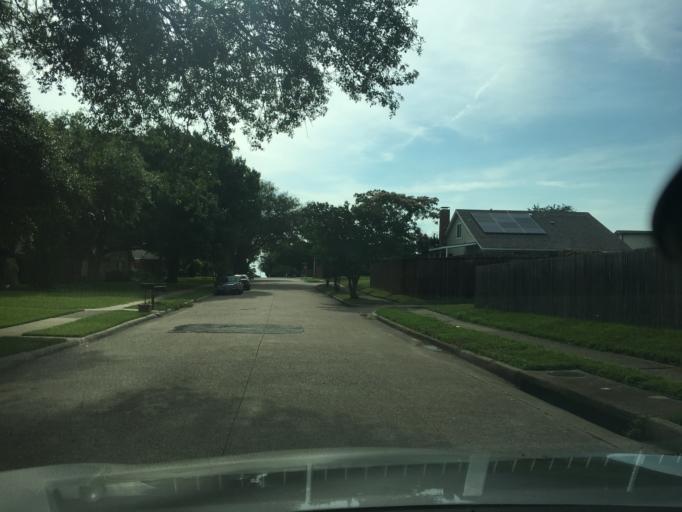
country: US
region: Texas
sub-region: Collin County
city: Plano
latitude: 32.9657
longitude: -96.6715
